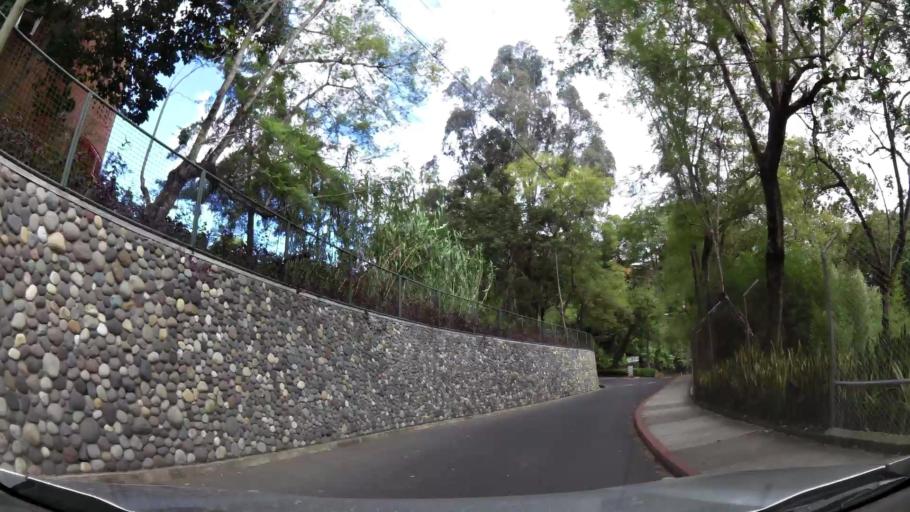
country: GT
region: Guatemala
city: Guatemala City
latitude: 14.6079
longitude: -90.5085
